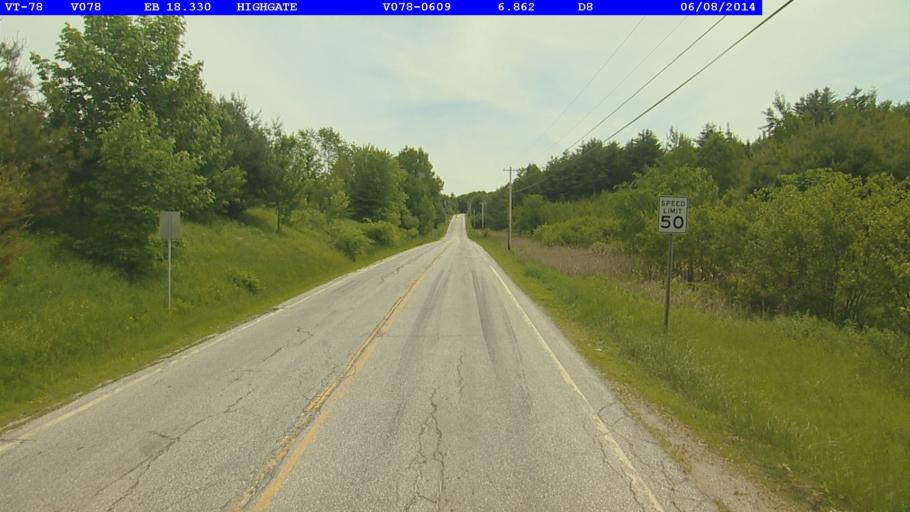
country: US
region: Vermont
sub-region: Franklin County
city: Swanton
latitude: 44.9270
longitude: -72.9839
